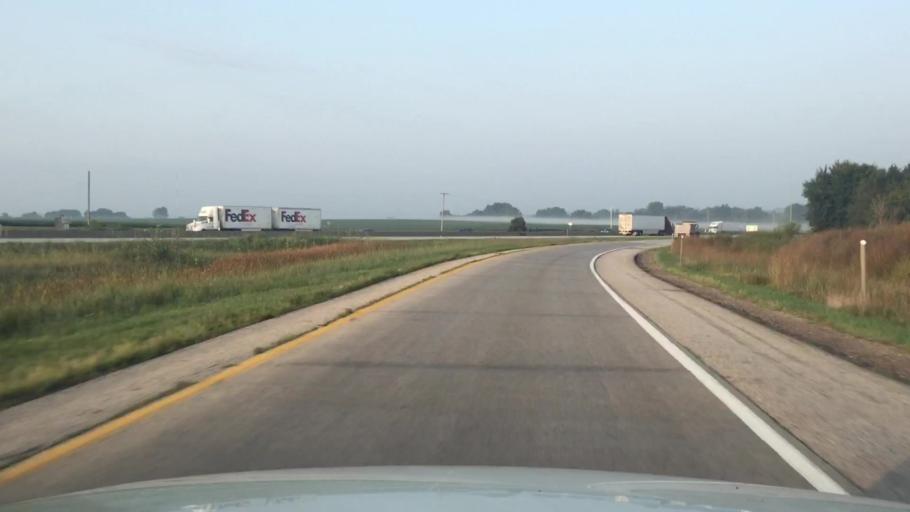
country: US
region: Iowa
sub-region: Polk County
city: Altoona
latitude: 41.6596
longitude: -93.5295
